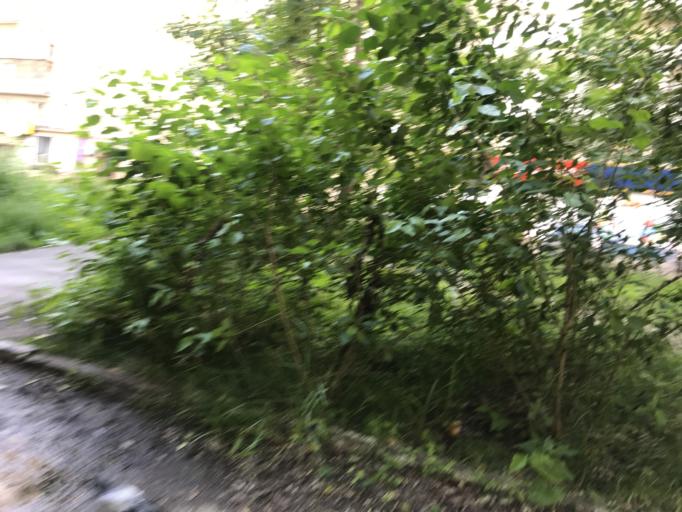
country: RU
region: Novosibirsk
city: Krasnoobsk
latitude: 54.9337
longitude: 82.9076
